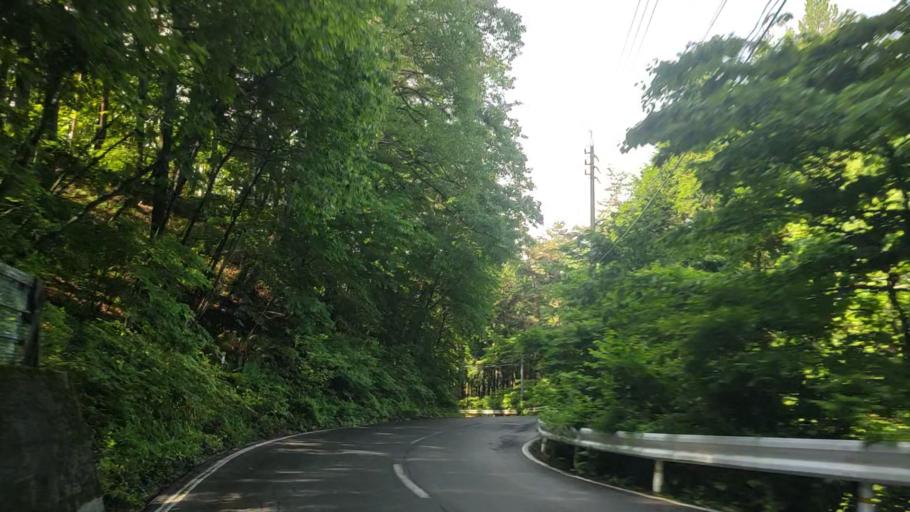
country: JP
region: Nagano
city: Suwa
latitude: 36.0765
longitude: 138.1386
